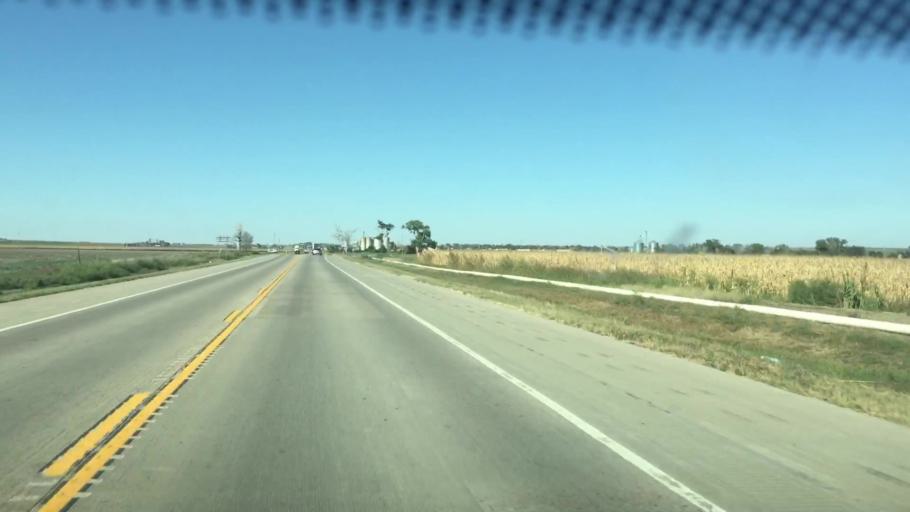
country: US
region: Colorado
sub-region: Prowers County
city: Lamar
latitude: 38.1383
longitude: -102.7237
